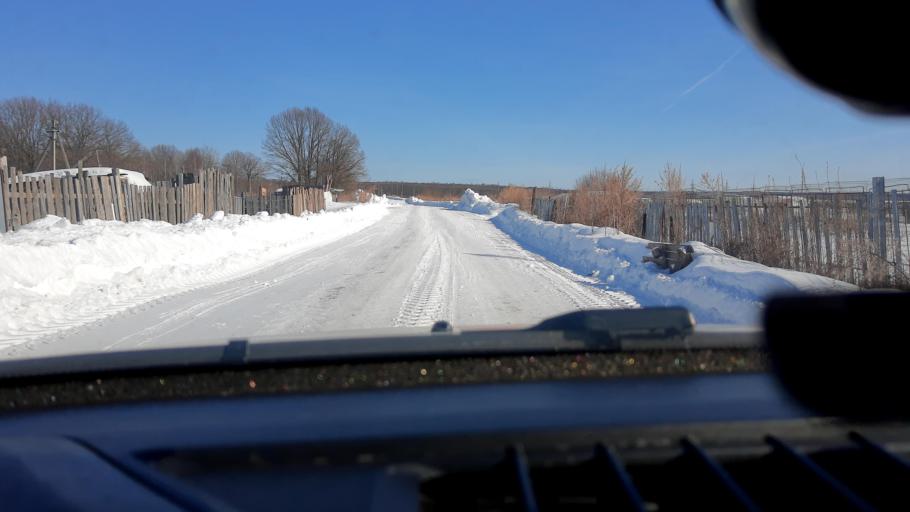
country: RU
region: Nizjnij Novgorod
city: Volodarsk
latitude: 56.2453
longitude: 43.1913
